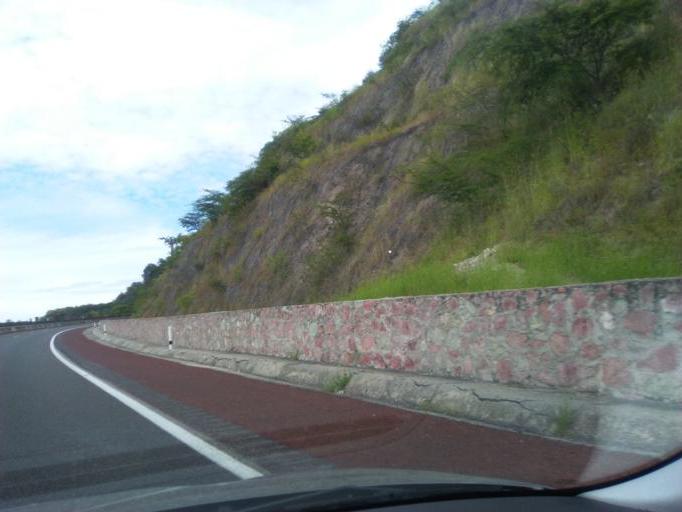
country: MX
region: Guerrero
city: Zumpango del Rio
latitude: 17.6917
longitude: -99.5063
